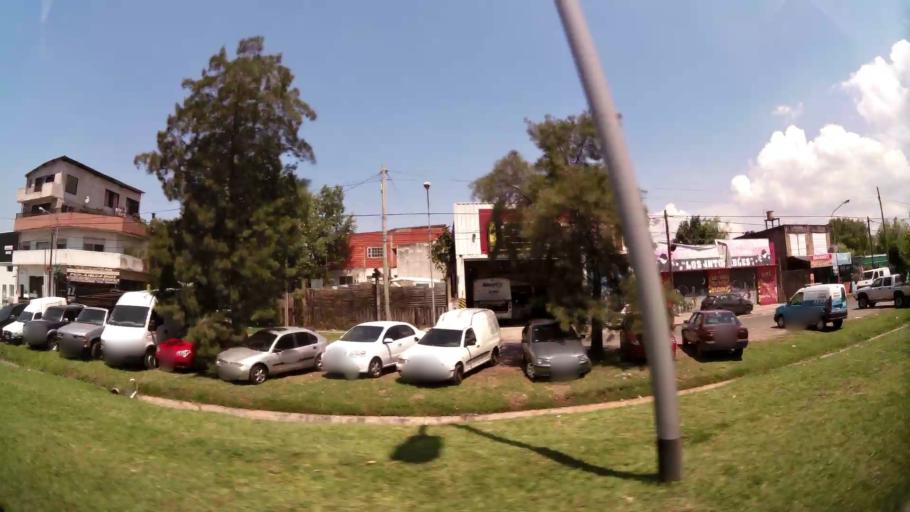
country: AR
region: Buenos Aires
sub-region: Partido de Tigre
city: Tigre
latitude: -34.4478
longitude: -58.6048
